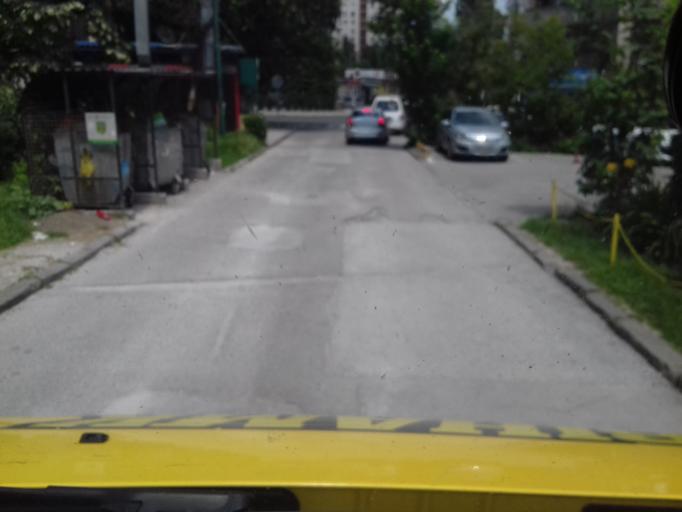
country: BA
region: Federation of Bosnia and Herzegovina
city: Kobilja Glava
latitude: 43.8508
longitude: 18.4023
